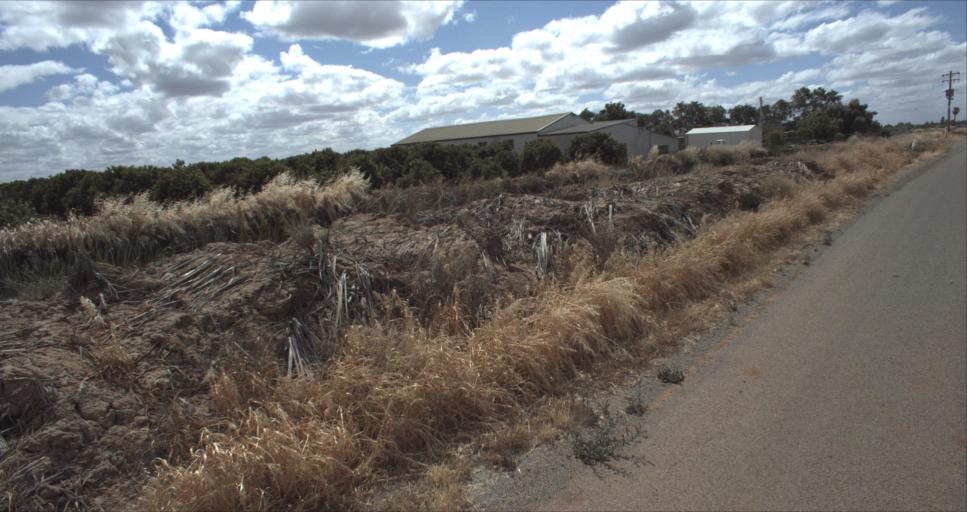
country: AU
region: New South Wales
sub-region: Leeton
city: Leeton
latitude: -34.5853
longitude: 146.3915
